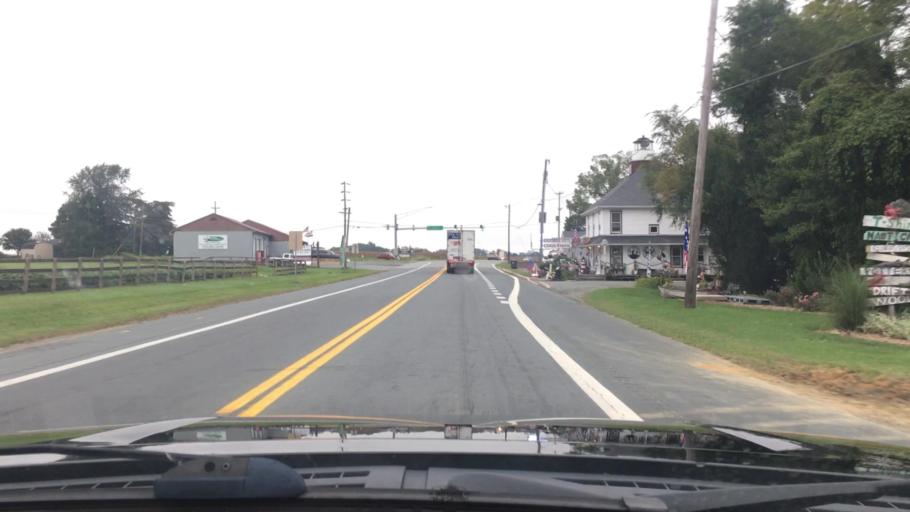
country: US
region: Maryland
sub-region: Cecil County
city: Elkton
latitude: 39.4849
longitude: -75.8482
